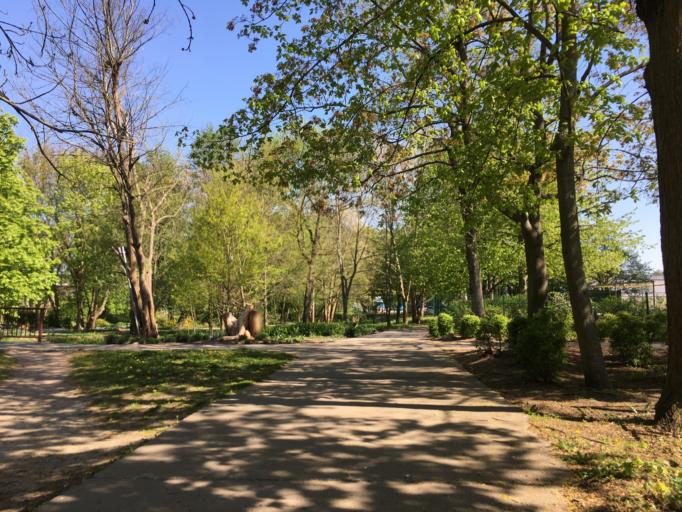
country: DE
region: Berlin
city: Buch
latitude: 52.6336
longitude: 13.4930
